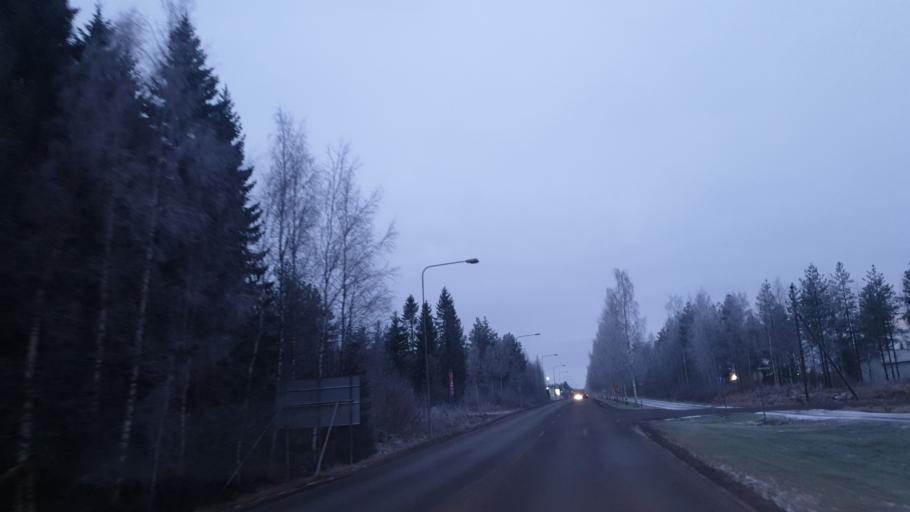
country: FI
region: Southern Ostrobothnia
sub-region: Seinaejoki
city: Nurmo
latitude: 62.7871
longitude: 22.9031
